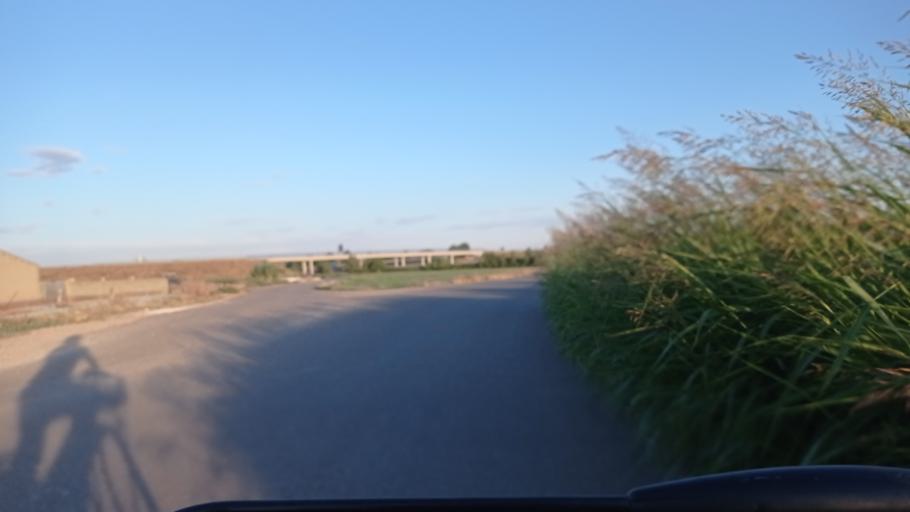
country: ES
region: Aragon
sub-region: Provincia de Zaragoza
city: Almozara
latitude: 41.6798
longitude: -0.9315
